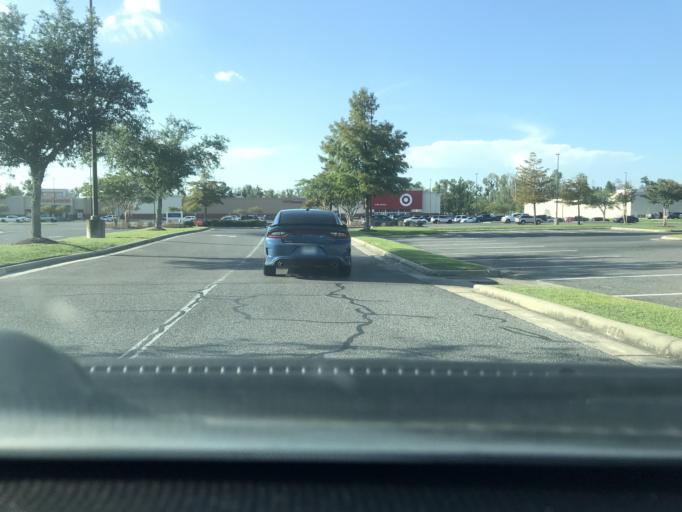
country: US
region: Louisiana
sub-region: Calcasieu Parish
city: Prien
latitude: 30.1981
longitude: -93.2464
